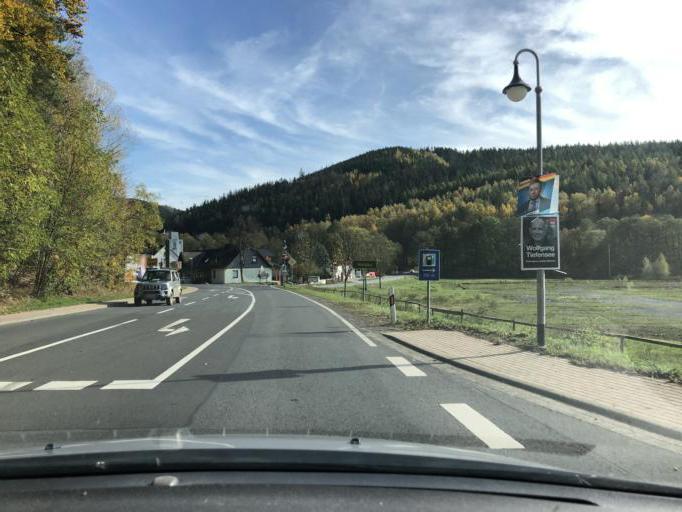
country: DE
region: Thuringia
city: Sankt Kilian
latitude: 50.5054
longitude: 10.8317
